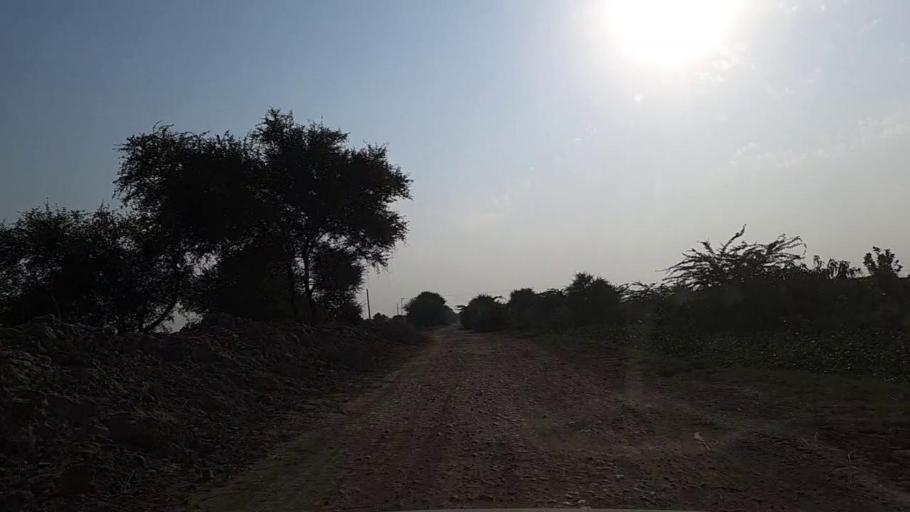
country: PK
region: Sindh
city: Mirpur Batoro
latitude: 24.7890
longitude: 68.2502
